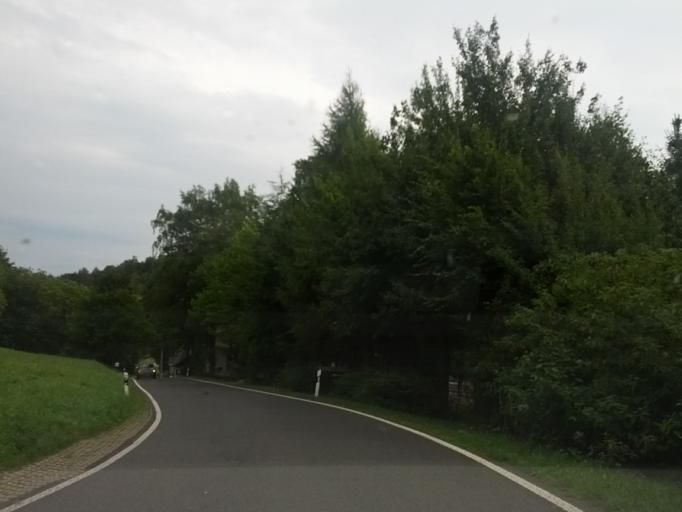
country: DE
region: Thuringia
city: Friedrichroda
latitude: 50.8648
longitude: 10.5873
